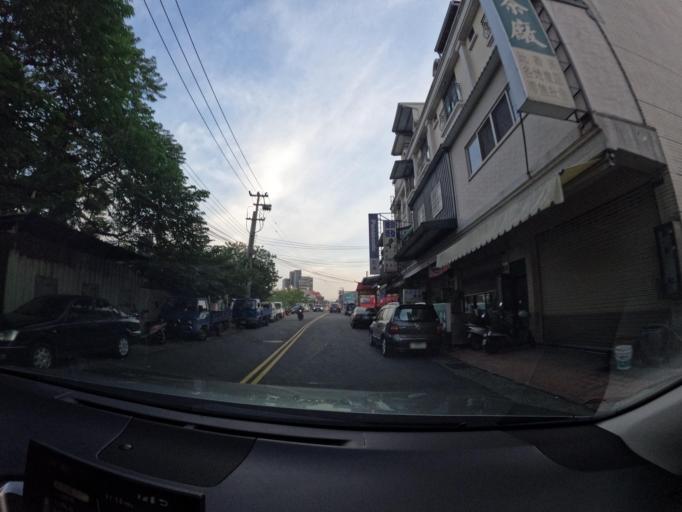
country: TW
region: Taiwan
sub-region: Taichung City
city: Taichung
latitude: 24.1182
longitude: 120.6847
